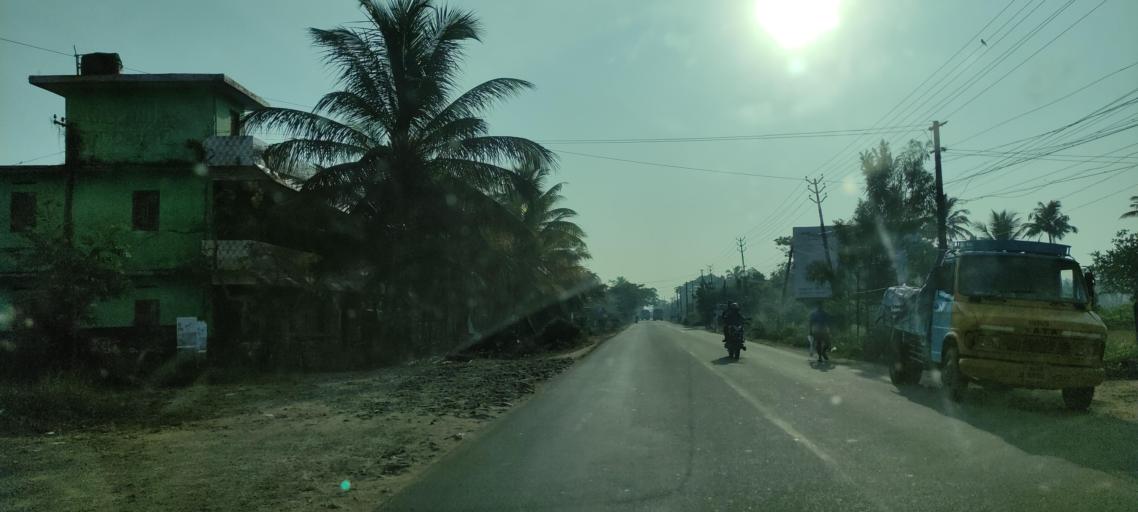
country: IN
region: Kerala
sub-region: Kottayam
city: Kottayam
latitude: 9.5924
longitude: 76.4414
